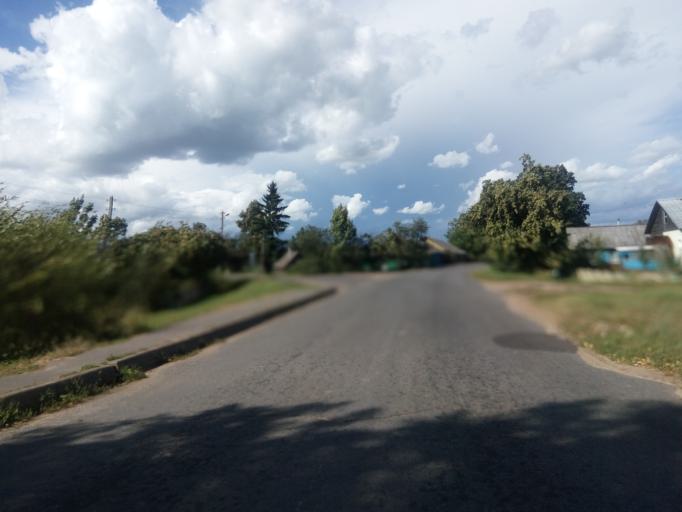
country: BY
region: Vitebsk
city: Dzisna
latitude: 55.7082
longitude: 28.1845
